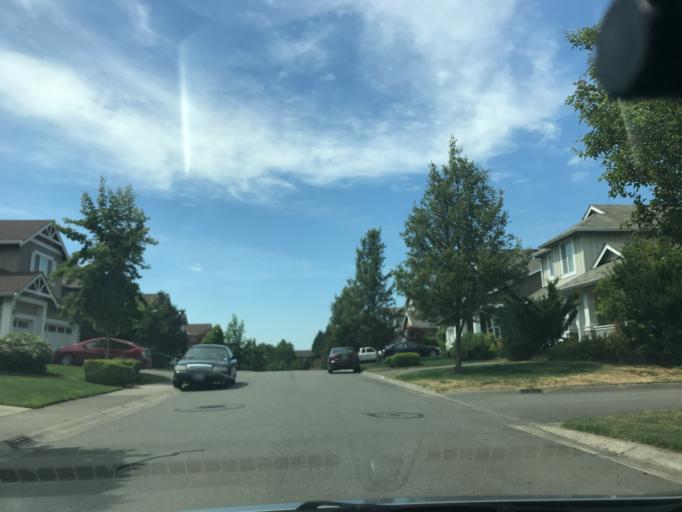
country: US
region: Washington
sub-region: King County
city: Ravensdale
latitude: 47.3508
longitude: -122.0065
